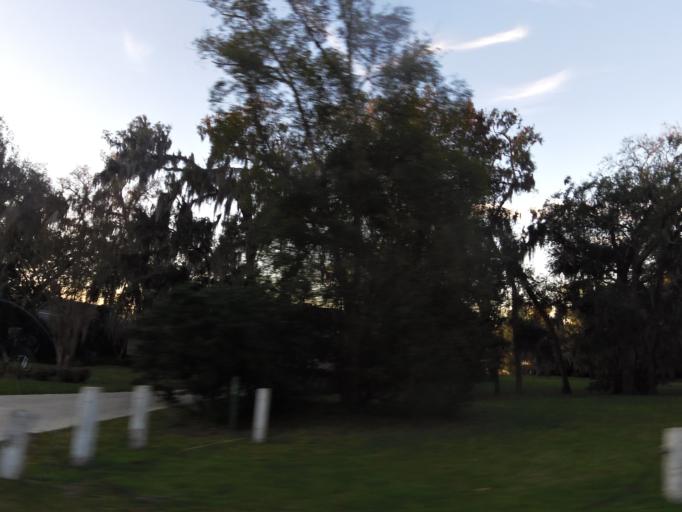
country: US
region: Florida
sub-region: Duval County
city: Jacksonville
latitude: 30.2729
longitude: -81.7075
